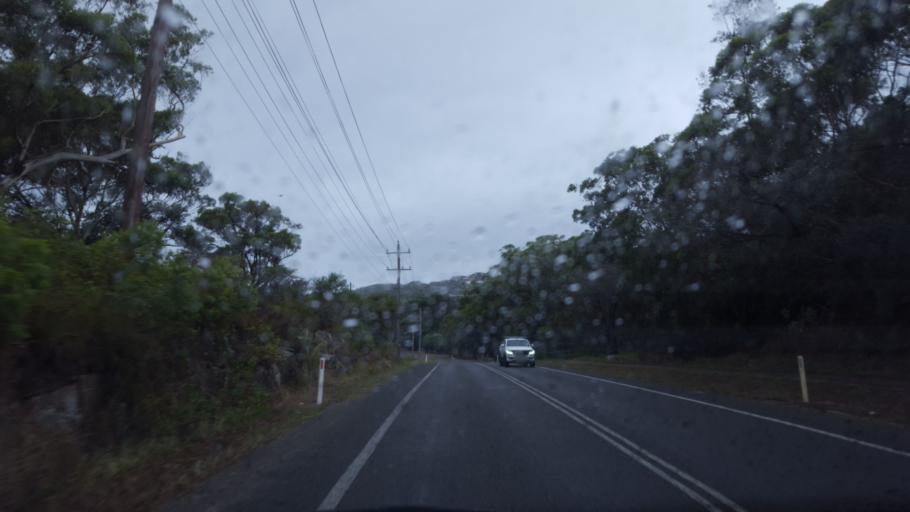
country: AU
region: New South Wales
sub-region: Port Stephens Shire
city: Anna Bay
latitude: -32.7780
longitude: 152.1035
